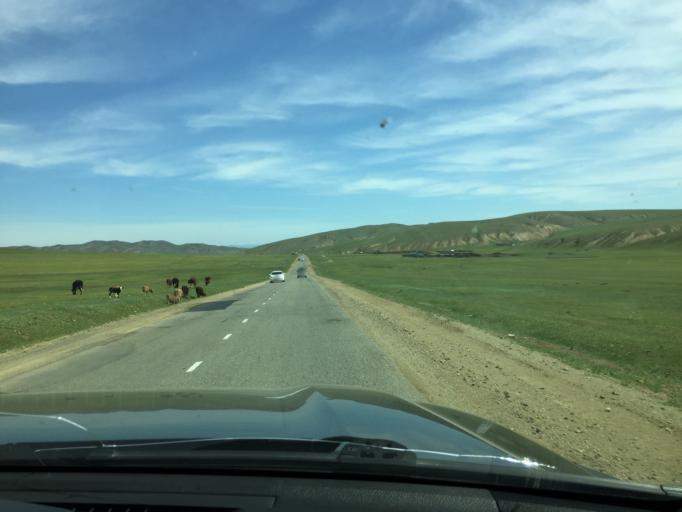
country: MN
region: Central Aimak
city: Bornuur
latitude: 48.6625
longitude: 106.1247
